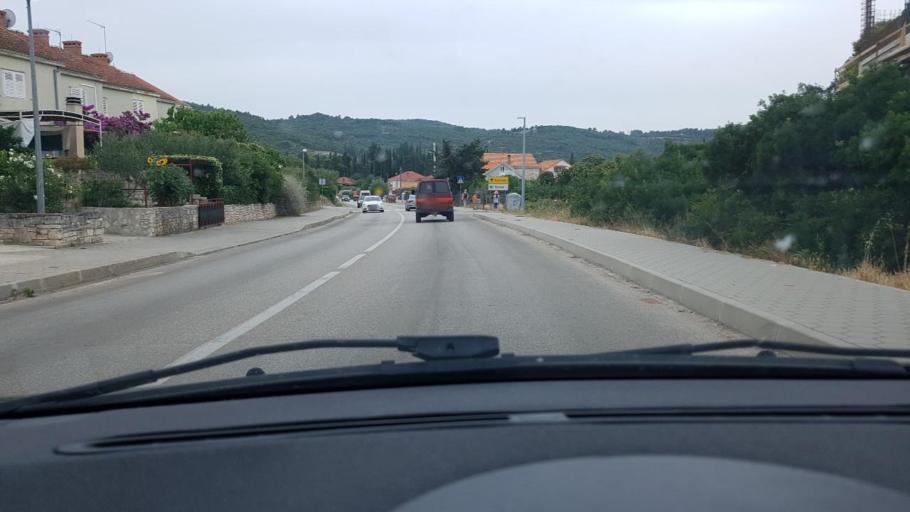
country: HR
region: Dubrovacko-Neretvanska
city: Korcula
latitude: 42.9494
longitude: 17.1411
